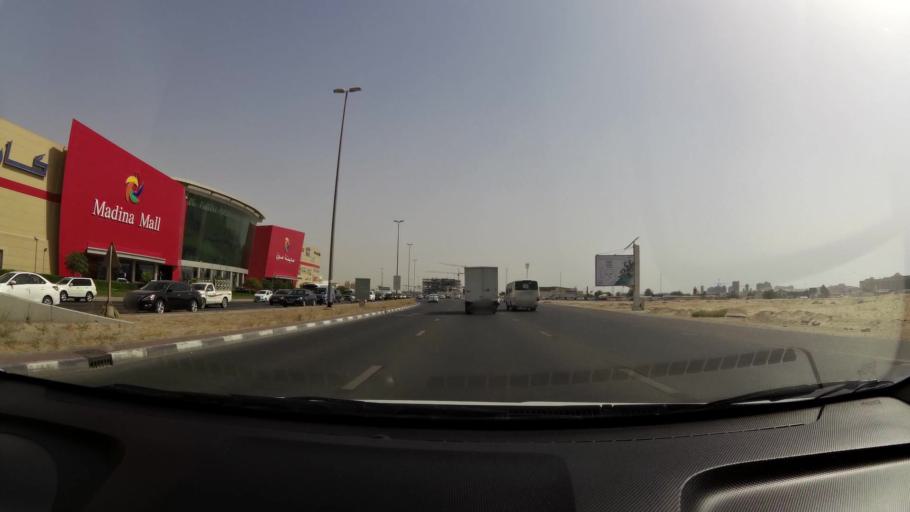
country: AE
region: Ash Shariqah
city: Sharjah
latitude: 25.2832
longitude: 55.3975
